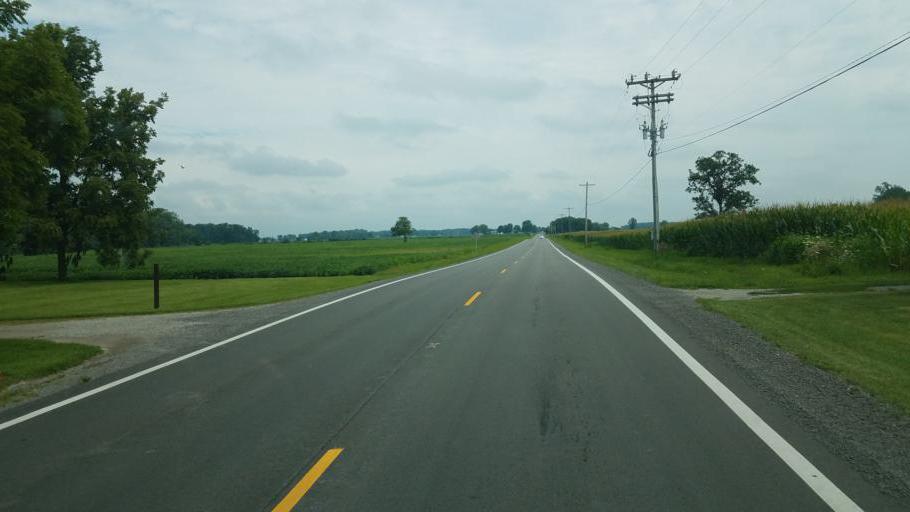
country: US
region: Ohio
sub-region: Marion County
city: Marion
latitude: 40.5280
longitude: -83.0563
